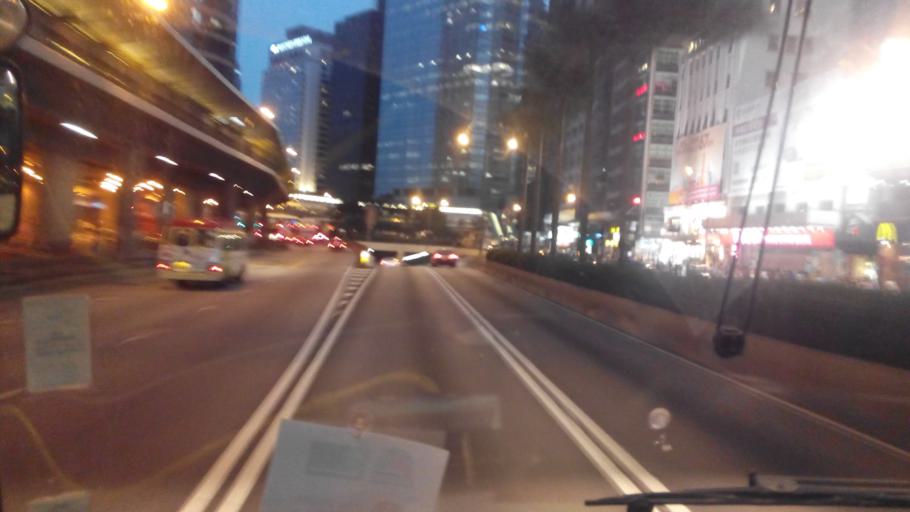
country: HK
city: Hong Kong
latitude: 22.2842
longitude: 114.1573
